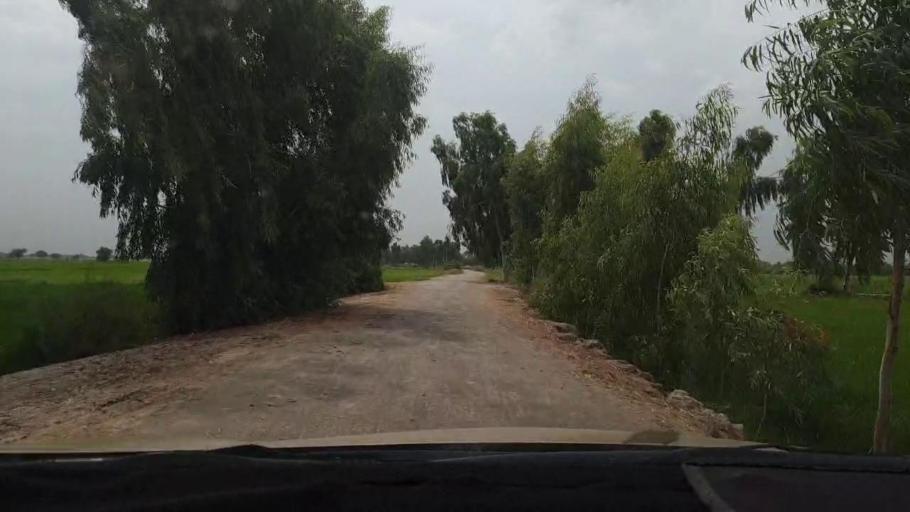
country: PK
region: Sindh
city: Naudero
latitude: 27.6247
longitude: 68.3237
